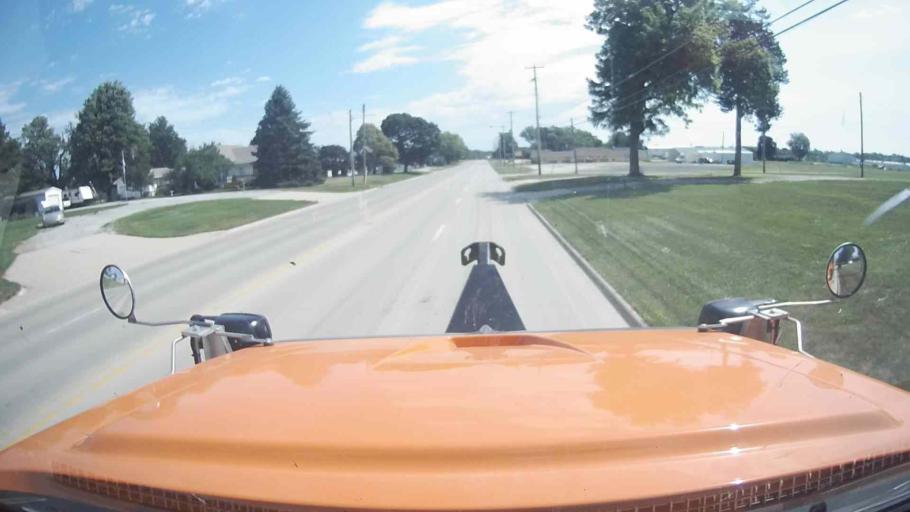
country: US
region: Iowa
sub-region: Union County
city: Creston
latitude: 41.0459
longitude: -94.3793
